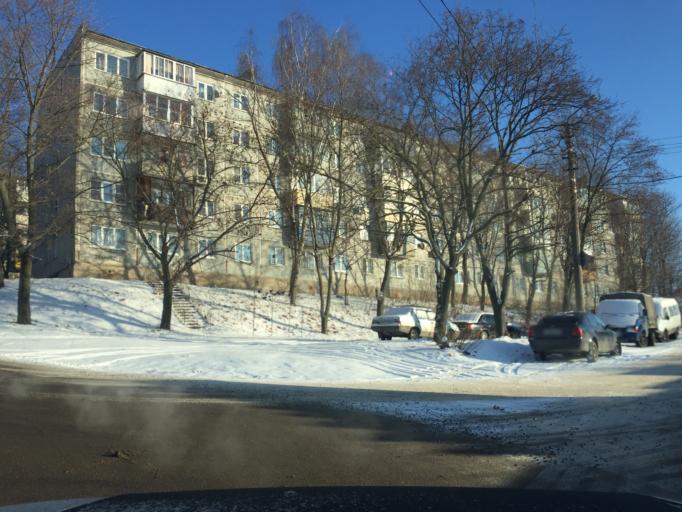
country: RU
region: Tula
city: Tula
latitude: 54.1895
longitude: 37.6832
